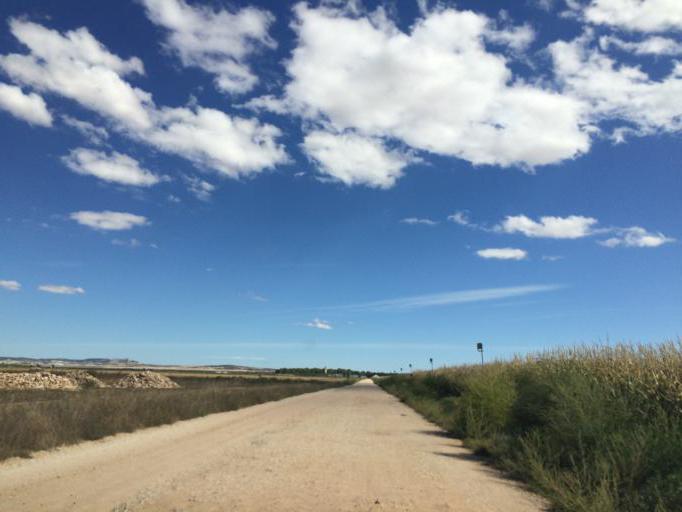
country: ES
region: Castille-La Mancha
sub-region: Provincia de Albacete
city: Albacete
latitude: 38.9357
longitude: -1.8806
